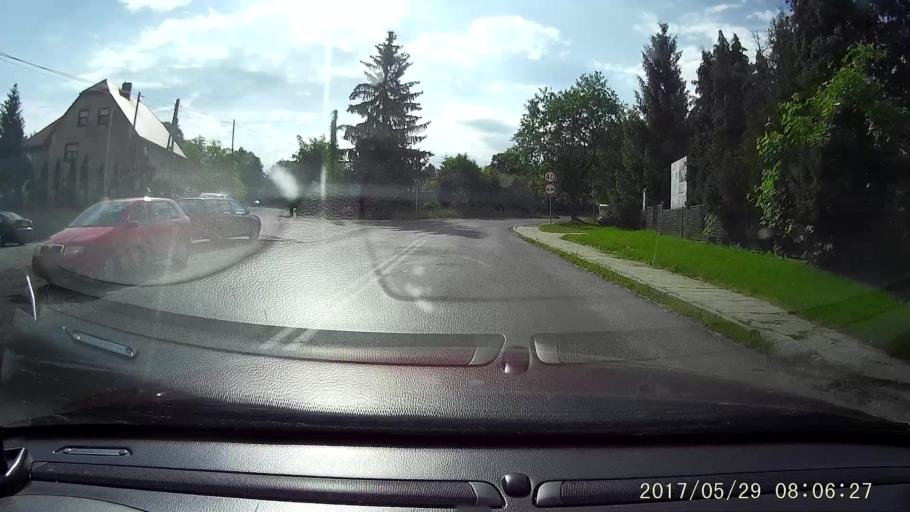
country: PL
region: Lower Silesian Voivodeship
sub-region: Powiat zlotoryjski
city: Zagrodno
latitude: 51.1903
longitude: 15.8662
